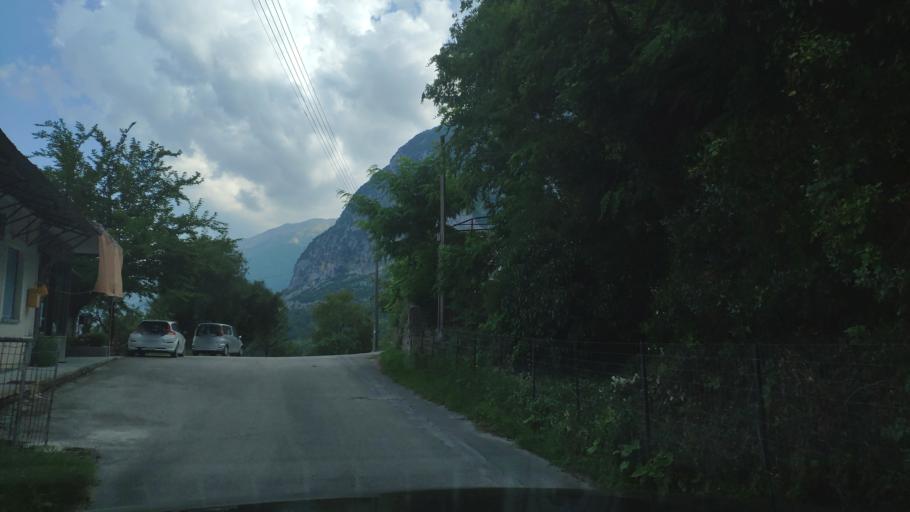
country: GR
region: Epirus
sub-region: Nomos Artas
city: Agios Dimitrios
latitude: 39.4450
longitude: 21.0170
